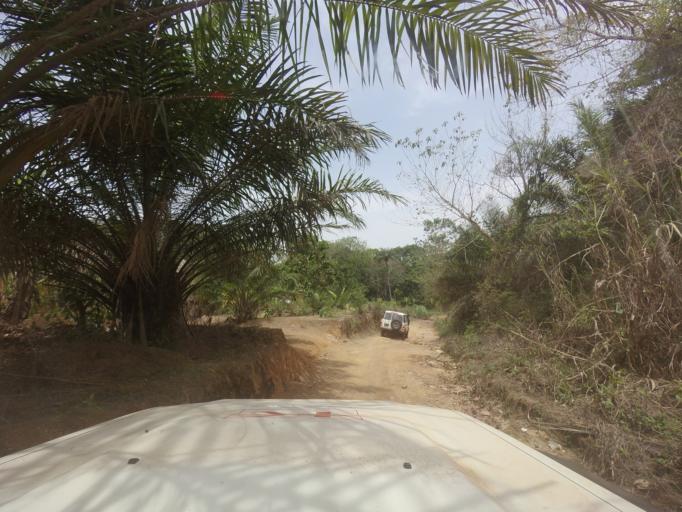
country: SL
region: Eastern Province
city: Buedu
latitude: 8.4779
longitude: -10.3370
